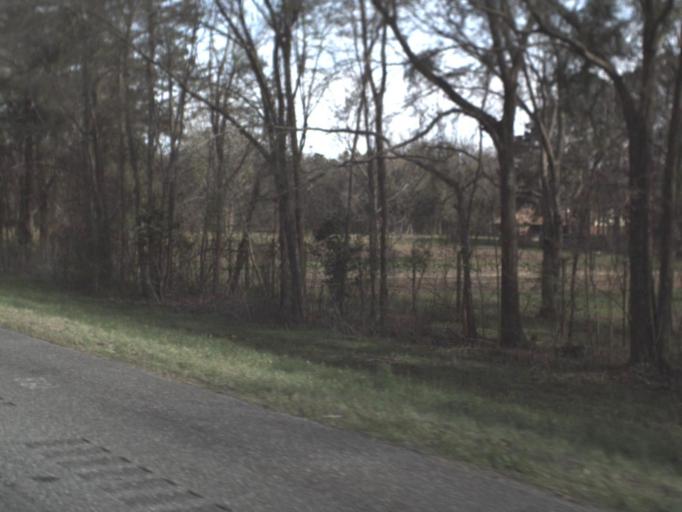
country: US
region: Florida
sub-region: Leon County
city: Tallahassee
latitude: 30.4780
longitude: -84.0805
